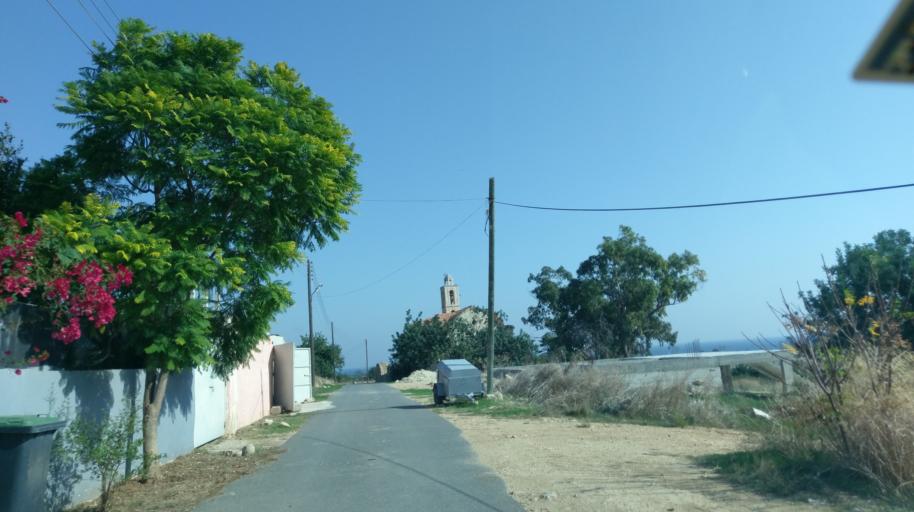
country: CY
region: Ammochostos
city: Leonarisso
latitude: 35.4297
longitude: 34.1342
